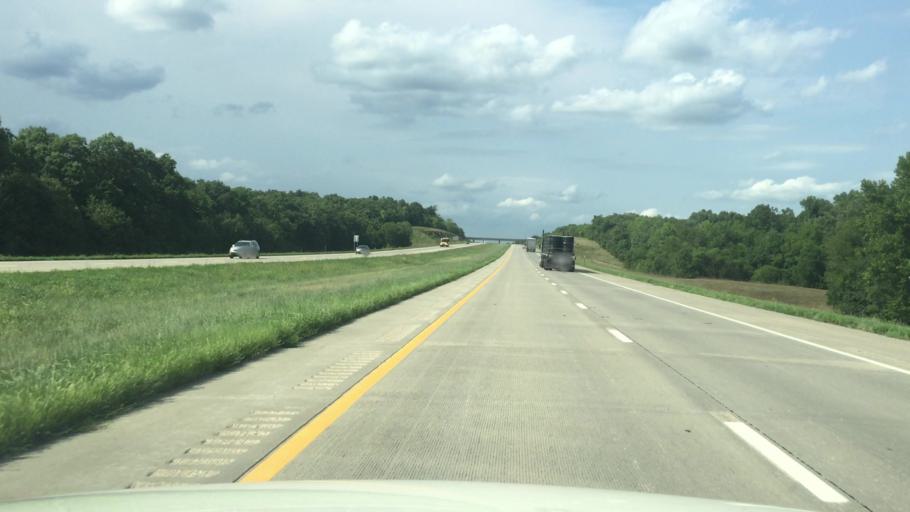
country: US
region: Kansas
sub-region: Miami County
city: Louisburg
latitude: 38.5973
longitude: -94.6940
